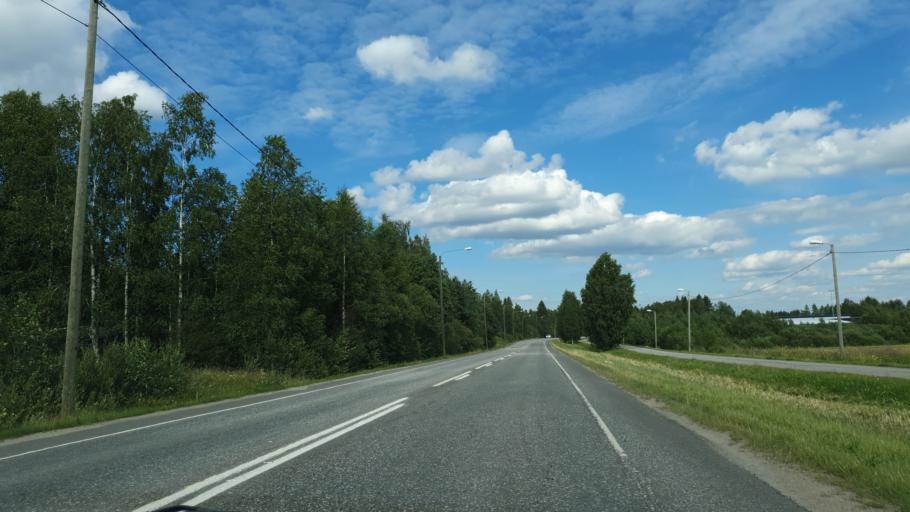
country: FI
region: Kainuu
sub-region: Kajaani
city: Kajaani
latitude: 64.2452
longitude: 27.7623
